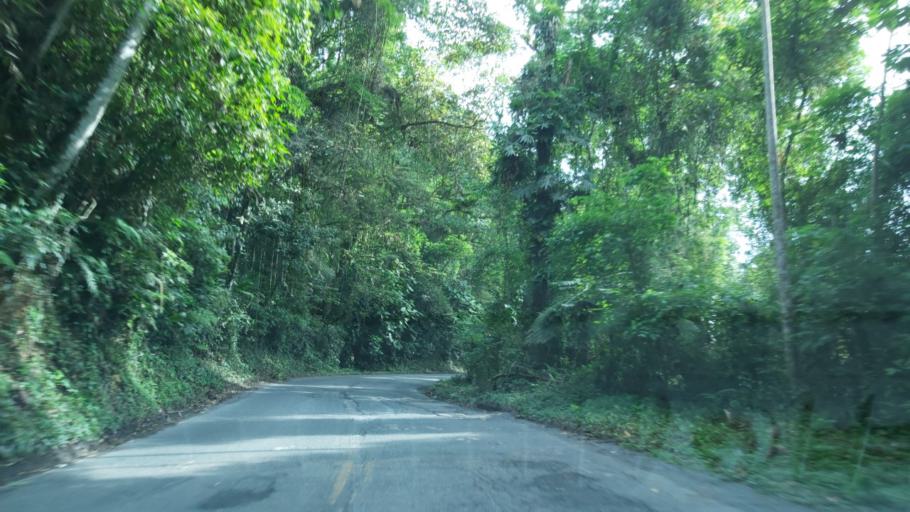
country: BR
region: Sao Paulo
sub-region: Juquia
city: Juquia
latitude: -24.0875
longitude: -47.6136
